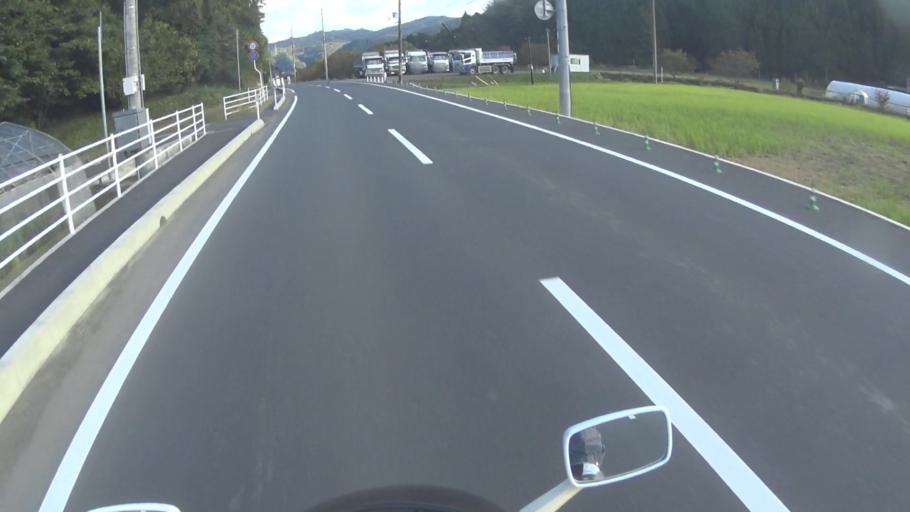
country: JP
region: Kyoto
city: Miyazu
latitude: 35.4349
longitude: 135.2248
